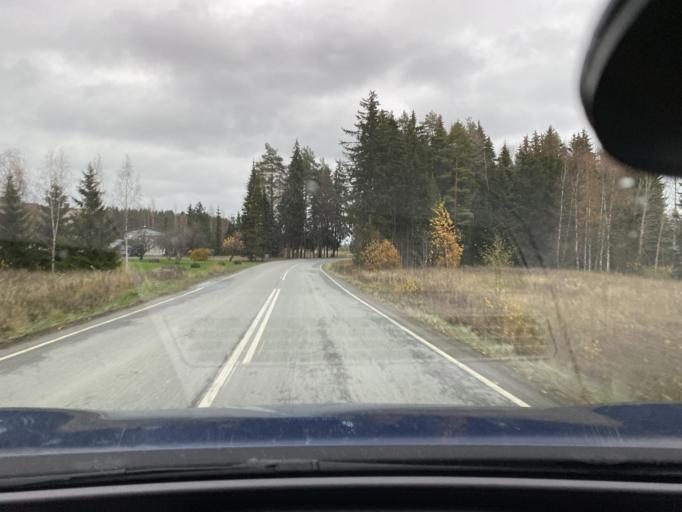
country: FI
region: Satakunta
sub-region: Pori
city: Huittinen
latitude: 61.1469
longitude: 22.6415
